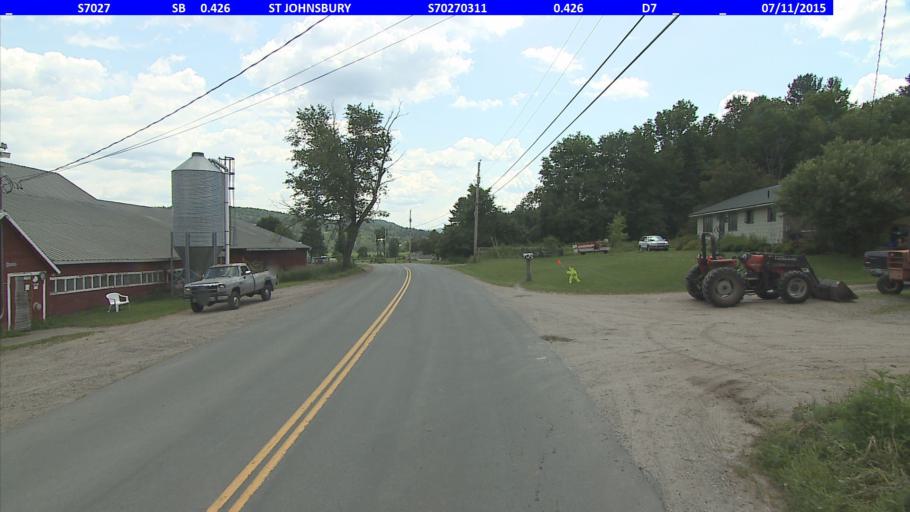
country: US
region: Vermont
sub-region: Caledonia County
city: St Johnsbury
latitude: 44.4538
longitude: -71.9455
